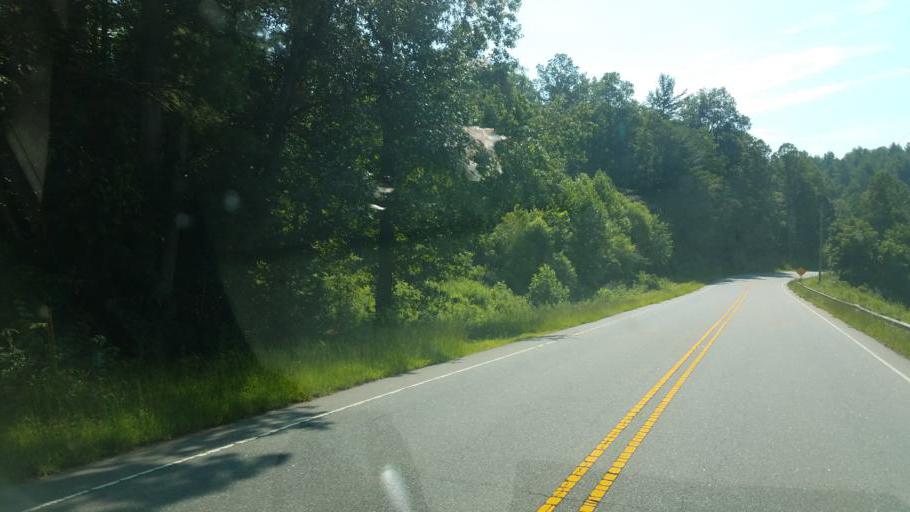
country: US
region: North Carolina
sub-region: Burke County
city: Glen Alpine
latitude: 35.8493
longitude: -81.7744
